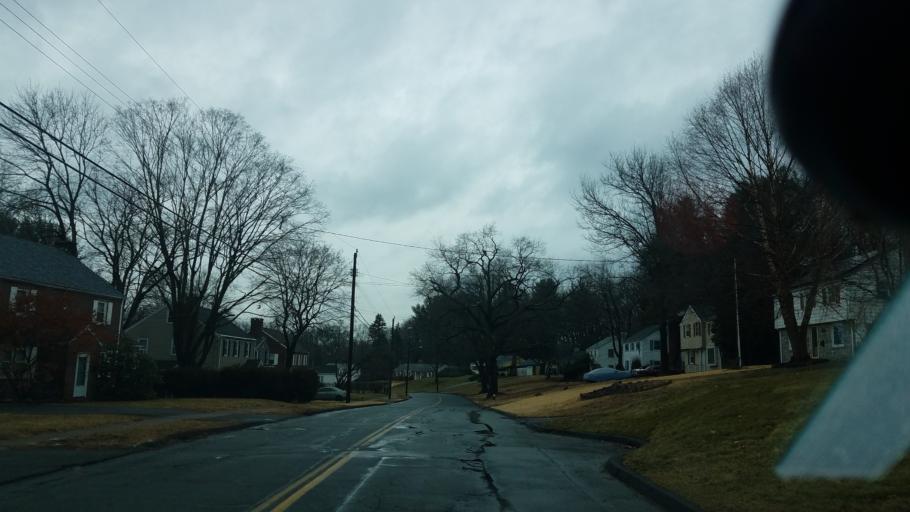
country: US
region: Connecticut
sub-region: Hartford County
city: East Hartford
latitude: 41.7691
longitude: -72.5938
